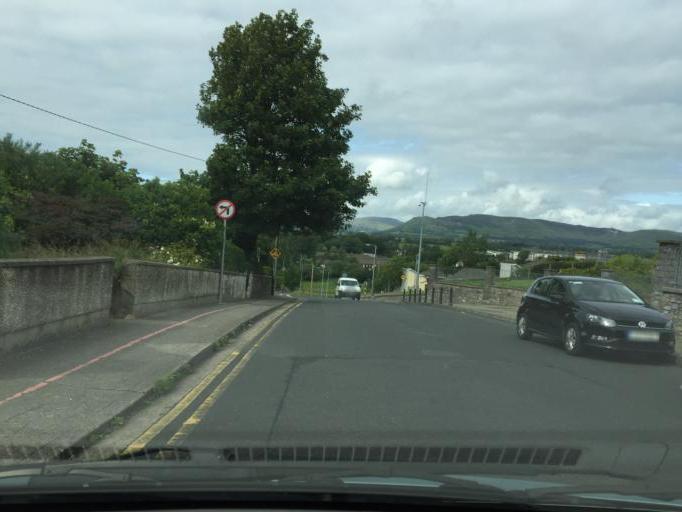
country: IE
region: Connaught
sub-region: Sligo
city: Sligo
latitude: 54.2764
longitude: -8.4721
